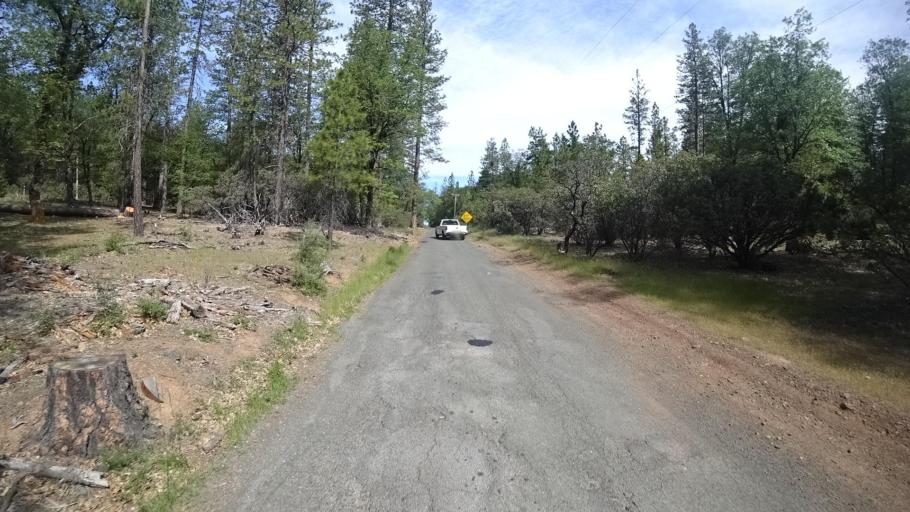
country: US
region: California
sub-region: Lake County
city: Cobb
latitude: 38.8909
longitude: -122.7849
